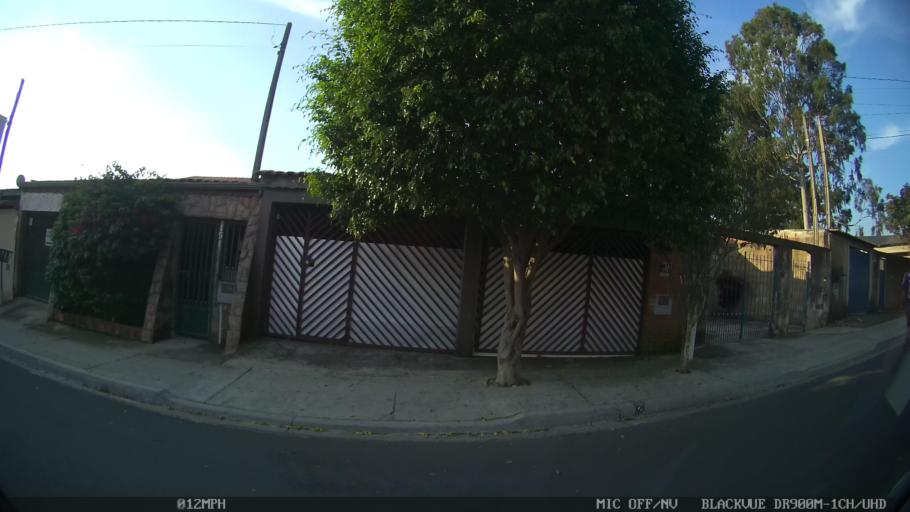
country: BR
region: Sao Paulo
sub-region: Campinas
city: Campinas
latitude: -22.9908
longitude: -47.1166
